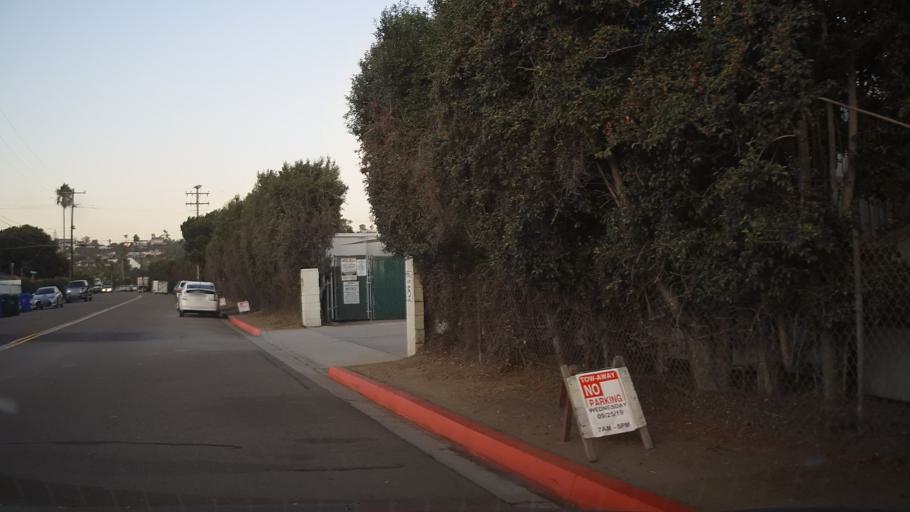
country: US
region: California
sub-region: San Diego County
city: San Diego
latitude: 32.7739
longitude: -117.2041
